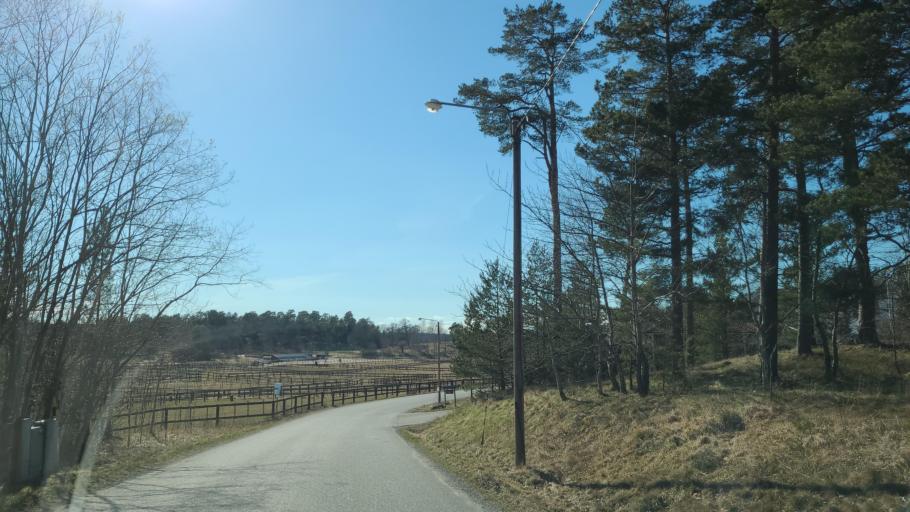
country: SE
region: Stockholm
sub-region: Varmdo Kommun
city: Hemmesta
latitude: 59.2777
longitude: 18.5587
